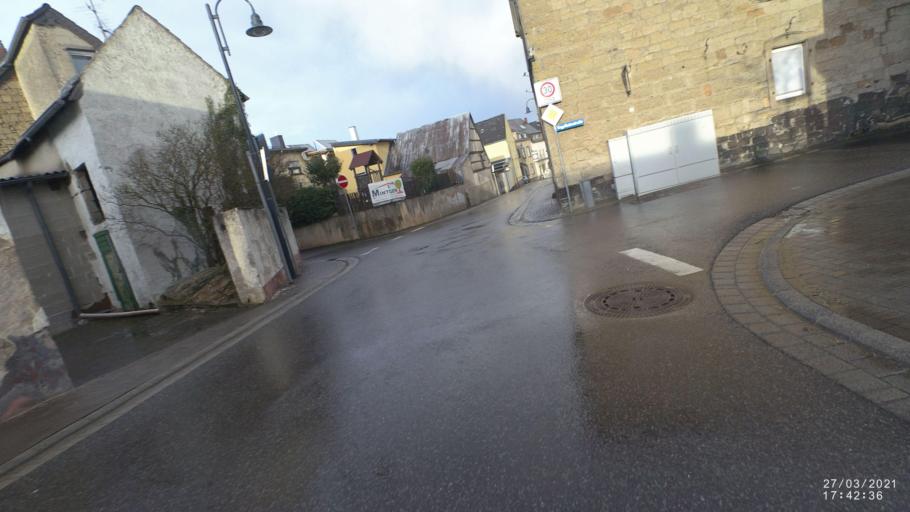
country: DE
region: Rheinland-Pfalz
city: Bell
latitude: 50.3875
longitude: 7.2330
